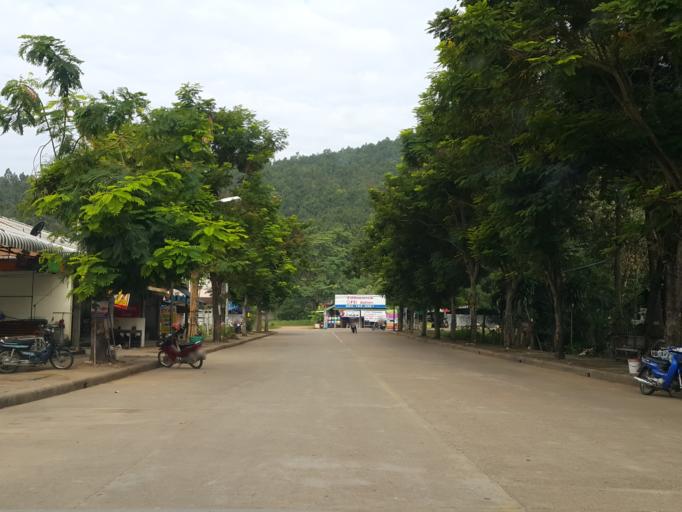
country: TH
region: Mae Hong Son
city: Mae Hong Son
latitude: 19.2932
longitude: 97.9627
